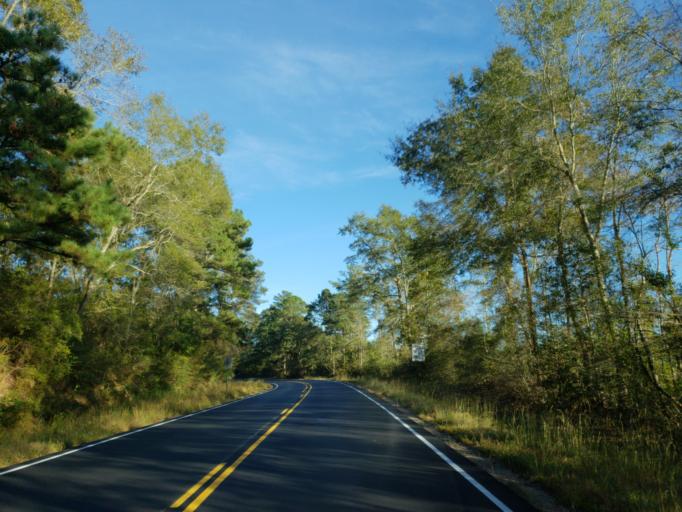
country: US
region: Mississippi
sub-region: Perry County
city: Richton
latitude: 31.3471
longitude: -88.7760
